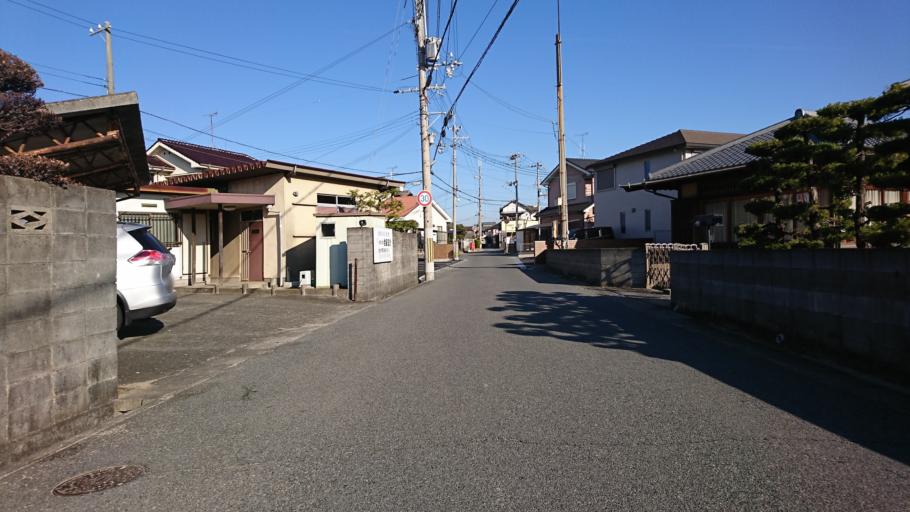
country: JP
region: Hyogo
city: Kakogawacho-honmachi
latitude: 34.7404
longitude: 134.8499
